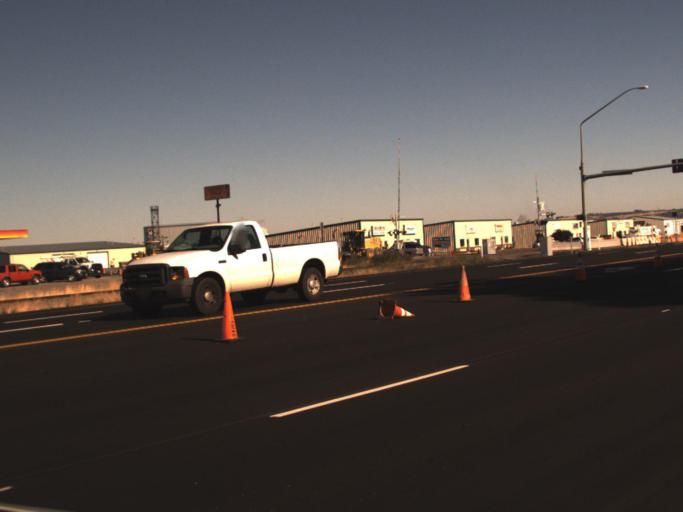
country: US
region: Washington
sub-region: Benton County
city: Richland
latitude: 46.2993
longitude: -119.2982
